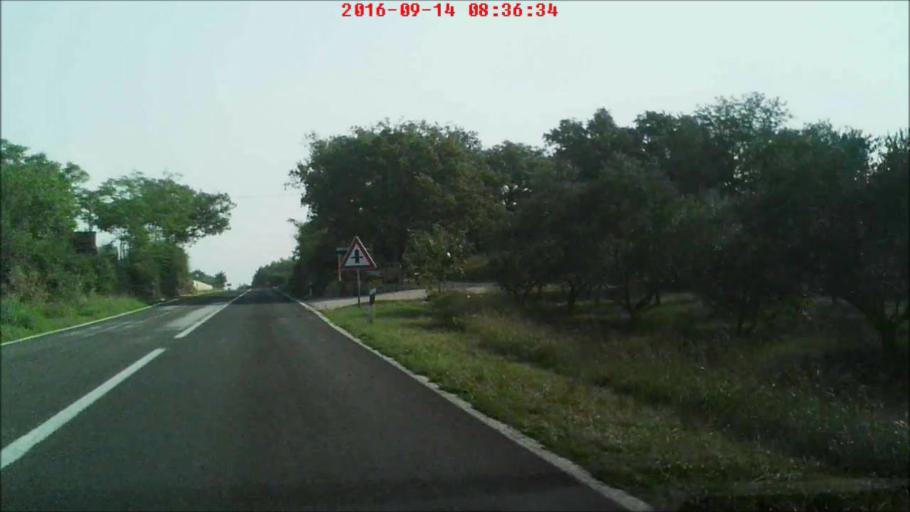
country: HR
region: Zadarska
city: Policnik
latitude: 44.1586
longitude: 15.3424
